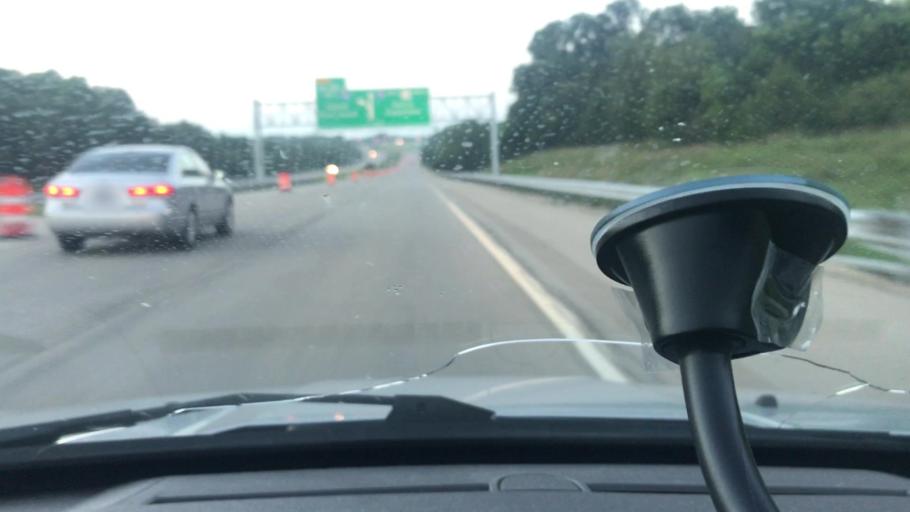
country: US
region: Illinois
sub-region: Peoria County
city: Bellevue
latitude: 40.7261
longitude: -89.6753
